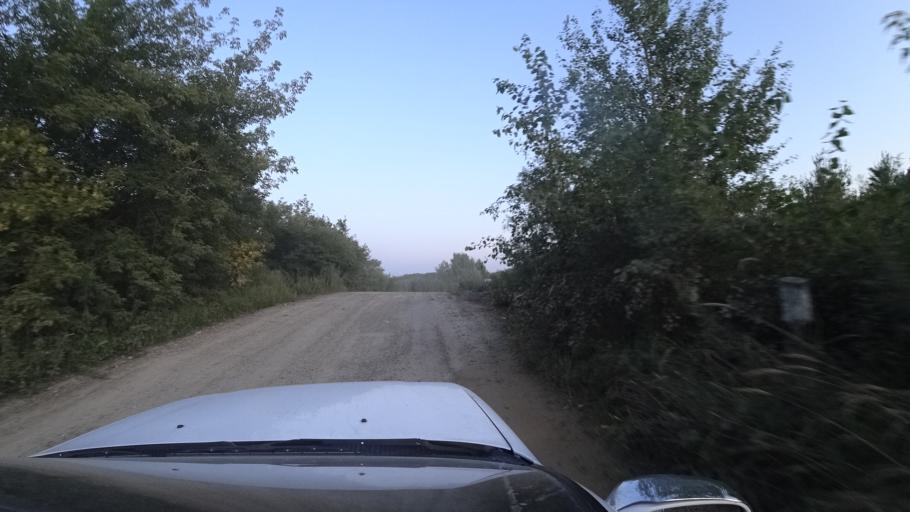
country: RU
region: Primorskiy
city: Dal'nerechensk
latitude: 45.9425
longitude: 133.7606
